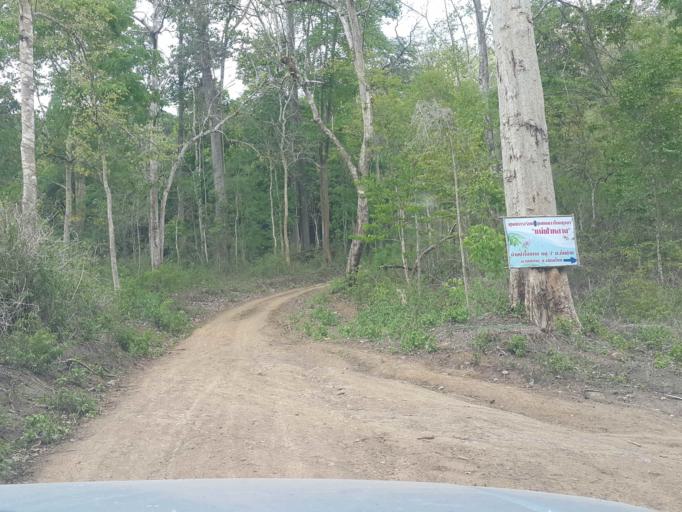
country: TH
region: Chiang Mai
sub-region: Amphoe Chiang Dao
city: Chiang Dao
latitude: 19.3163
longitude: 98.7270
